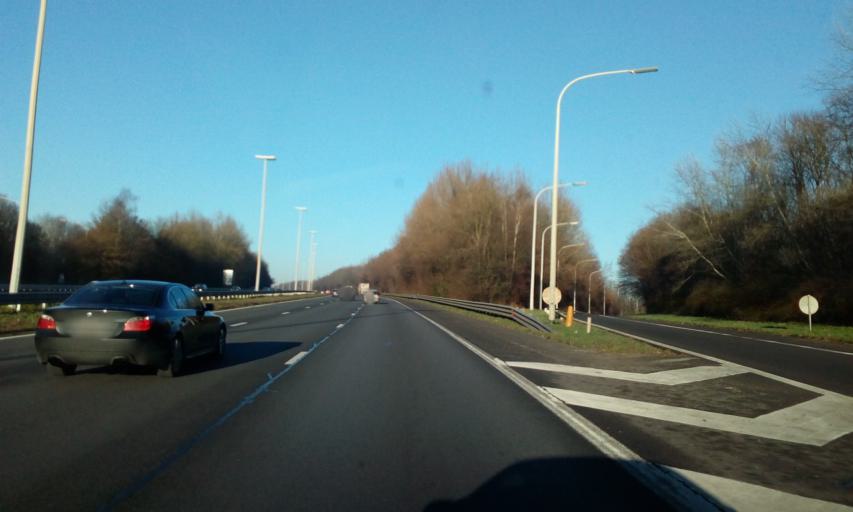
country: BE
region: Wallonia
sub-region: Province du Brabant Wallon
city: Nivelles
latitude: 50.6230
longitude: 4.3060
